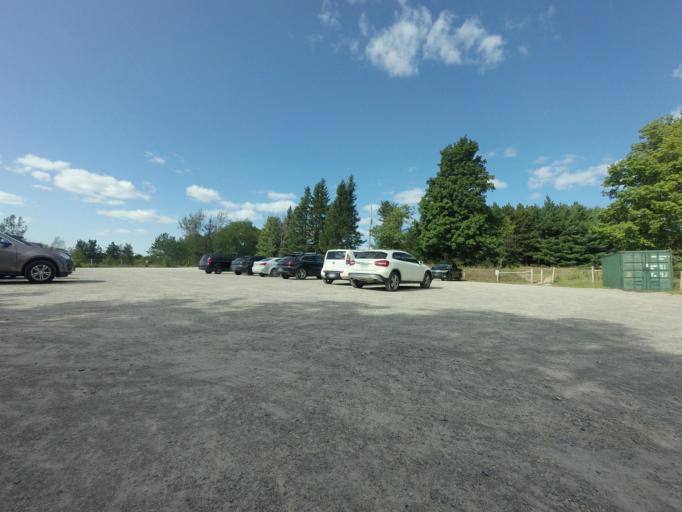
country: CA
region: Ontario
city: Orangeville
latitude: 43.8246
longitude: -80.0040
